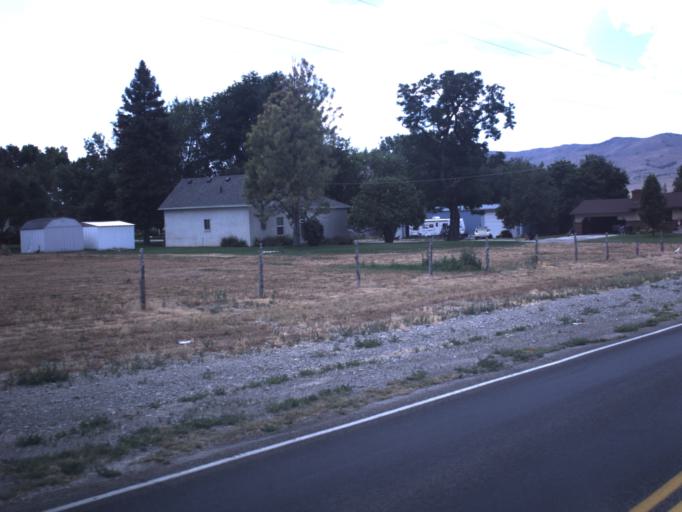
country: US
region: Utah
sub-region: Juab County
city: Mona
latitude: 39.8191
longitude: -111.8524
